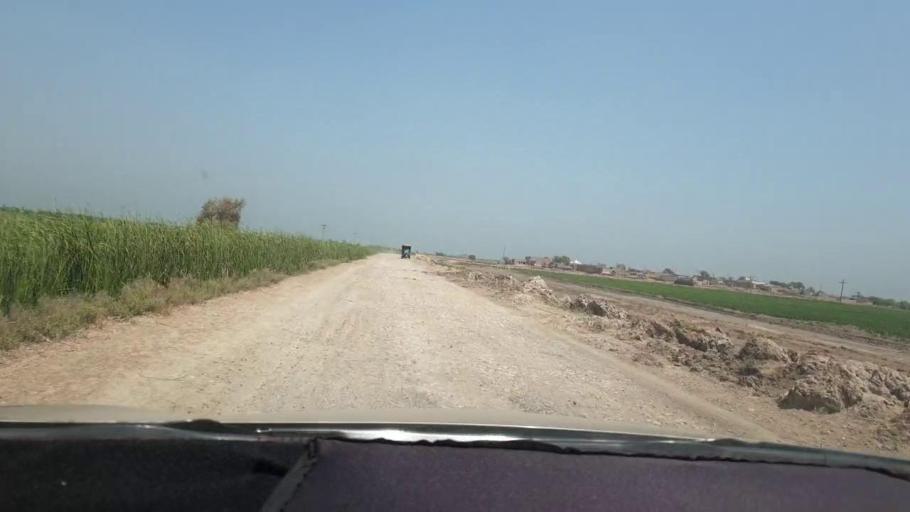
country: PK
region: Sindh
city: Shahdadkot
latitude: 27.8377
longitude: 67.9986
